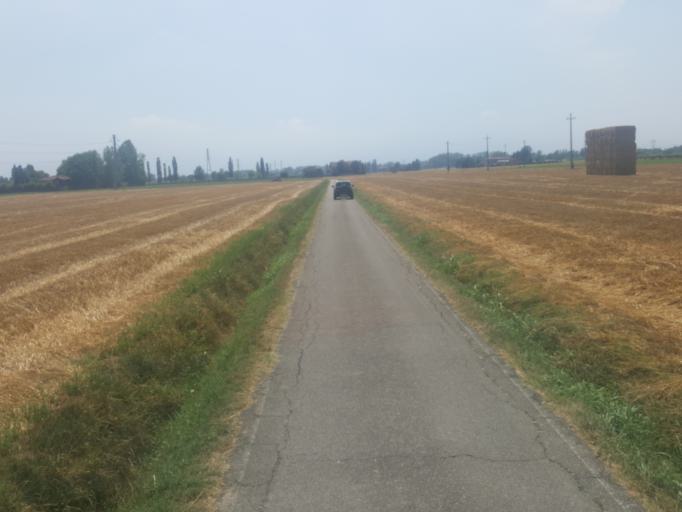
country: IT
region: Emilia-Romagna
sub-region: Provincia di Modena
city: Gaggio
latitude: 44.6451
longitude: 11.0011
